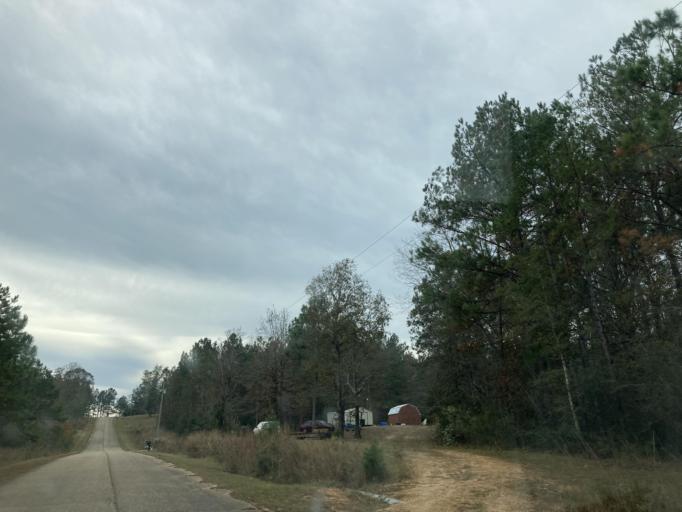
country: US
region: Mississippi
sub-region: Lamar County
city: Purvis
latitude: 31.1176
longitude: -89.4485
